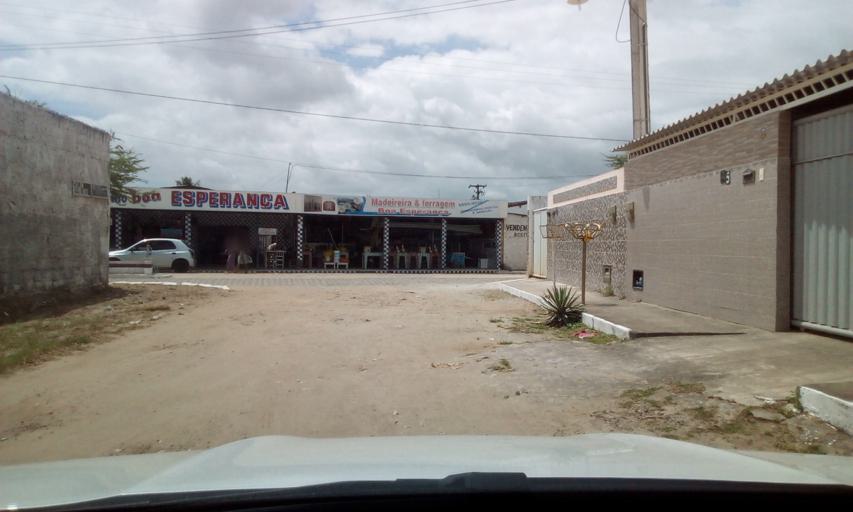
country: BR
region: Paraiba
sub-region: Bayeux
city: Bayeux
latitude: -7.1335
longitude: -34.9528
